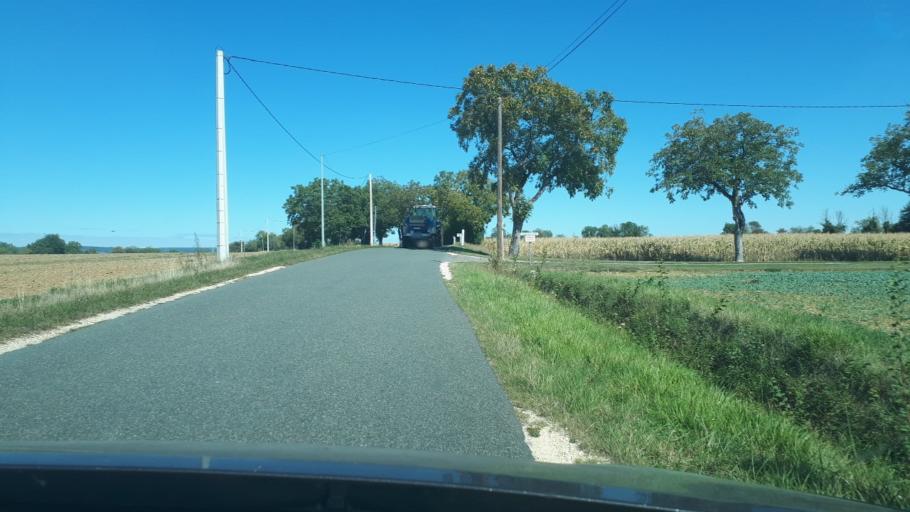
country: FR
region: Centre
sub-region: Departement du Cher
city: Sainte-Solange
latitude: 47.1605
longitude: 2.5670
